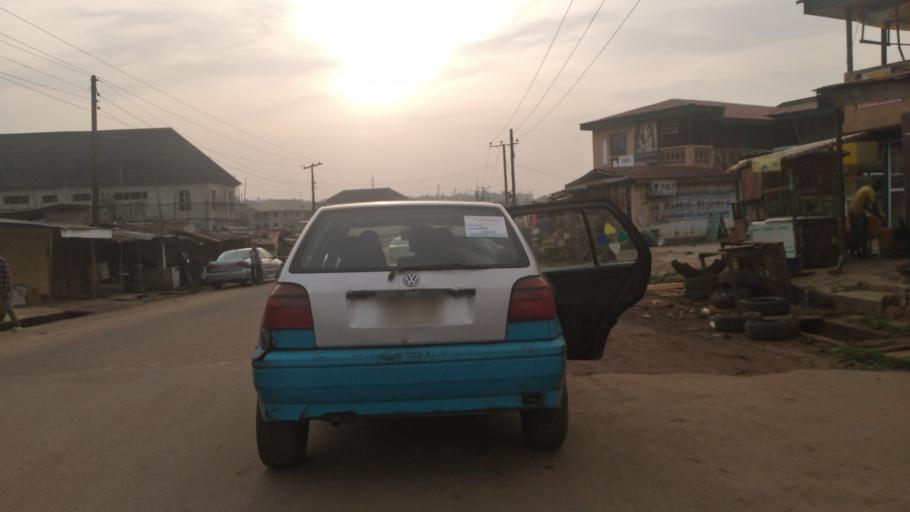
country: NG
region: Ondo
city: Akure
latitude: 7.2927
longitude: 5.1514
